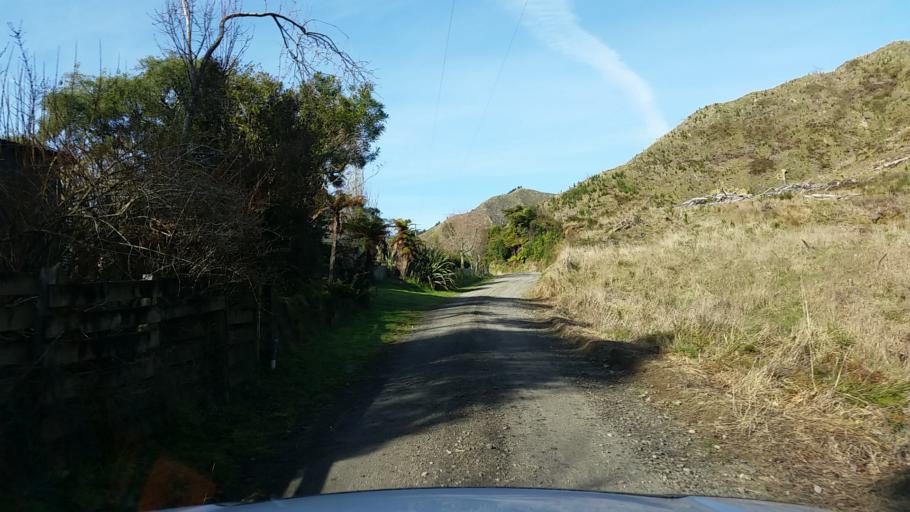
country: NZ
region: Taranaki
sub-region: South Taranaki District
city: Eltham
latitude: -39.3599
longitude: 174.5129
